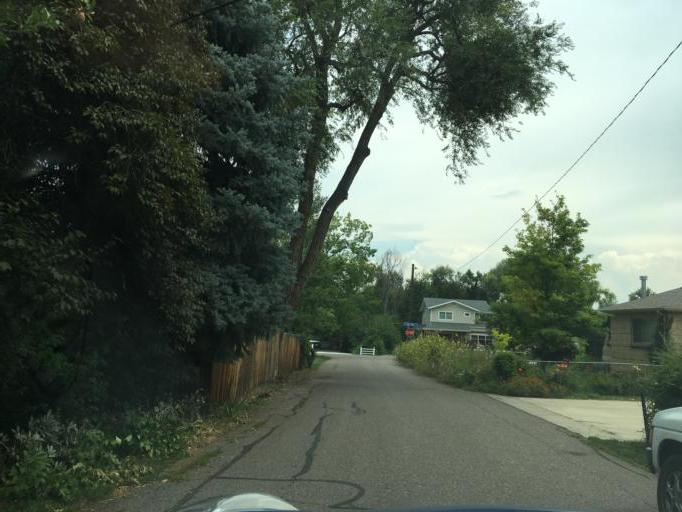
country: US
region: Colorado
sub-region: Jefferson County
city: Wheat Ridge
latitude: 39.7462
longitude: -105.0969
